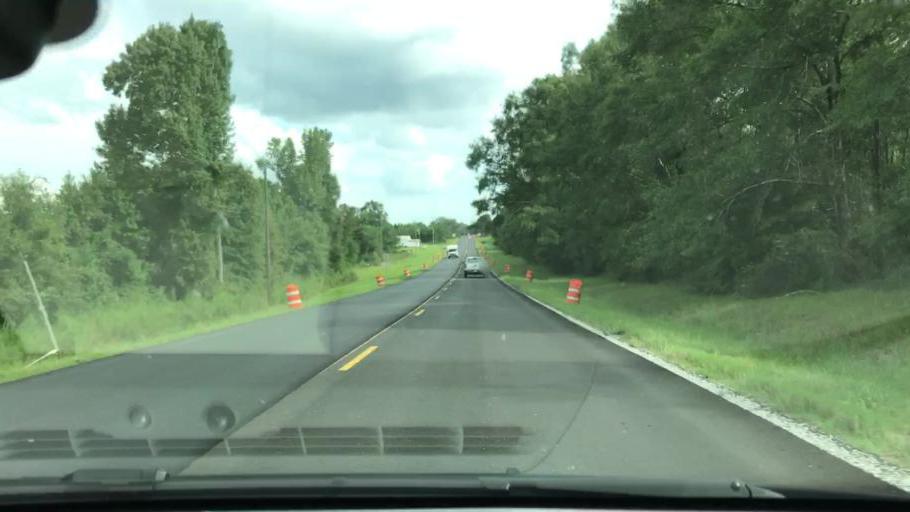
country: US
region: Georgia
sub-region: Clay County
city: Fort Gaines
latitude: 31.5843
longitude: -85.0270
